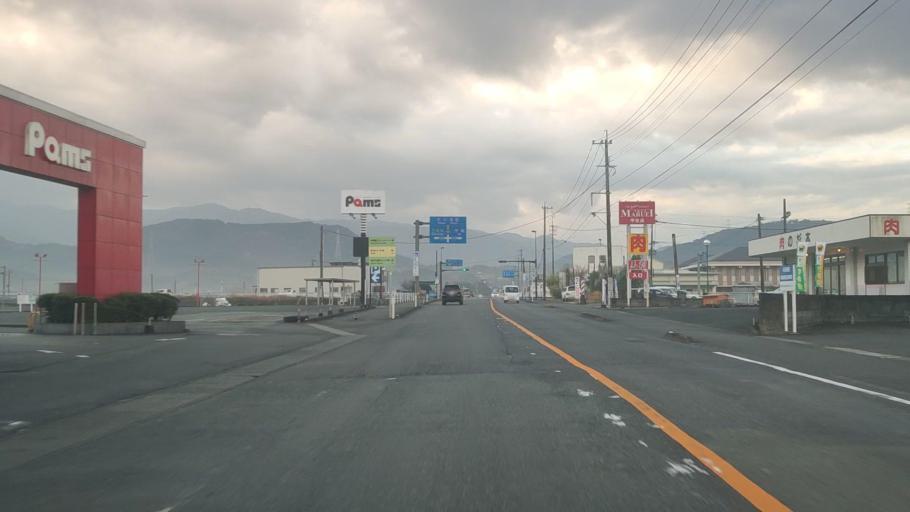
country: JP
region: Kumamoto
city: Matsubase
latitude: 32.6491
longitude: 130.8112
